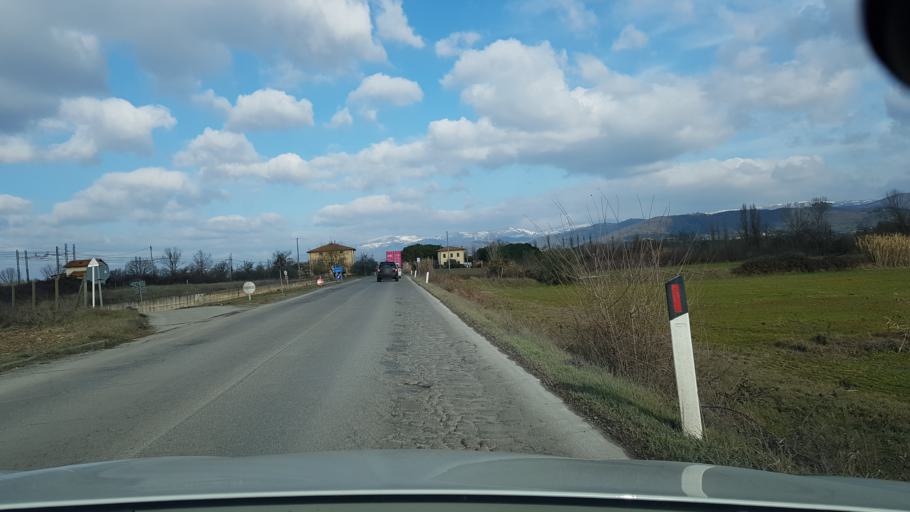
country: IT
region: Tuscany
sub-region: Province of Arezzo
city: Terontola
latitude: 43.1733
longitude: 12.0141
